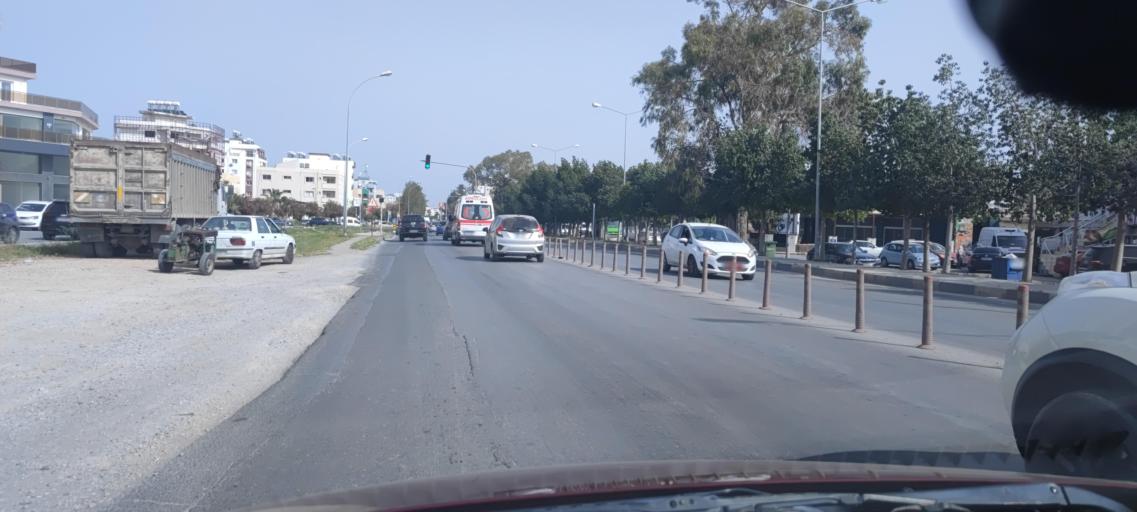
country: CY
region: Ammochostos
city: Famagusta
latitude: 35.1263
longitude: 33.9253
